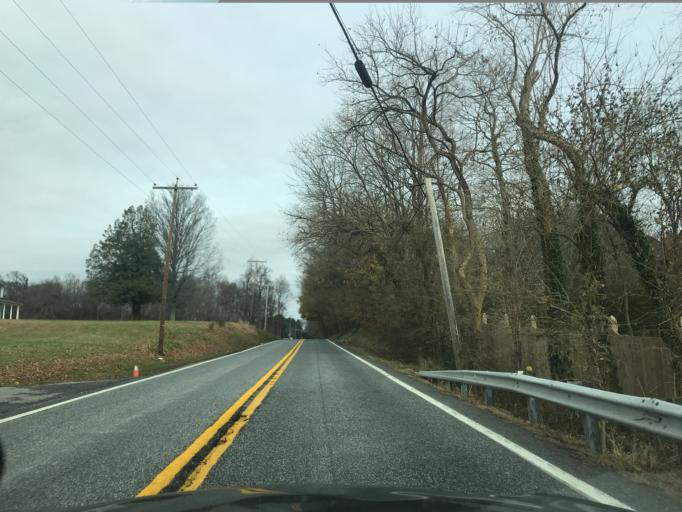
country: US
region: Maryland
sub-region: Harford County
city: Jarrettsville
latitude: 39.5838
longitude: -76.5127
